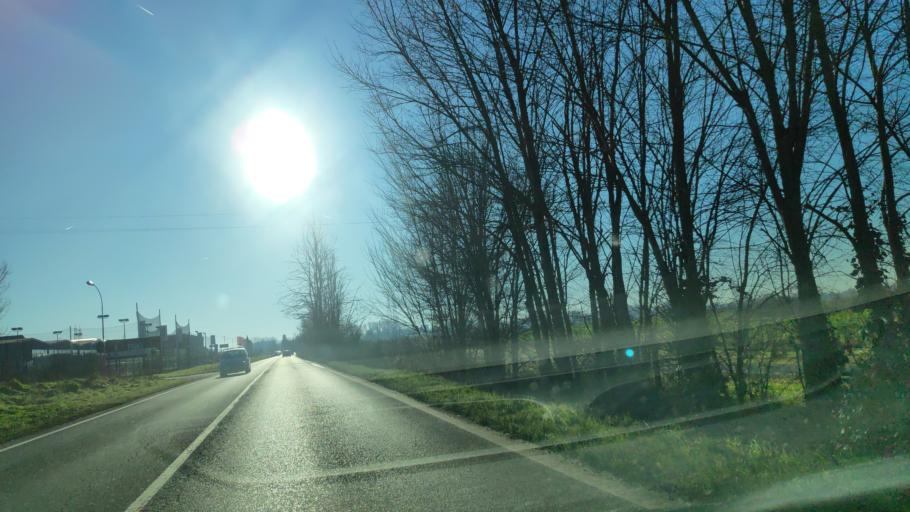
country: IT
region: Lombardy
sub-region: Citta metropolitana di Milano
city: Colturano
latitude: 45.3769
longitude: 9.3381
